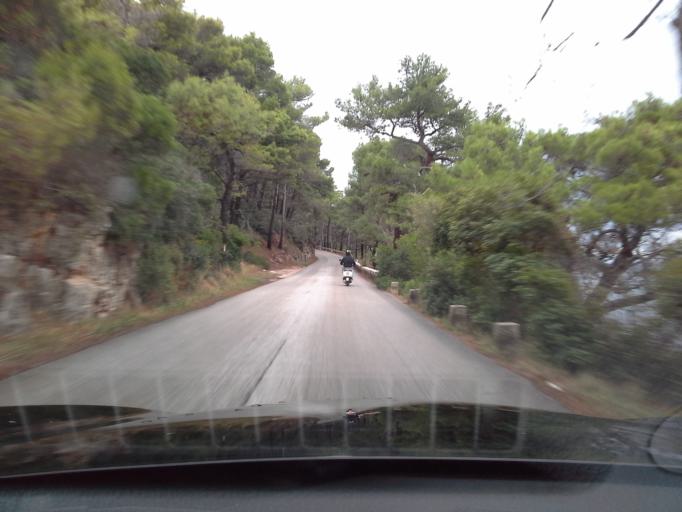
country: HR
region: Primorsko-Goranska
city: Mali Losinj
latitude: 44.5243
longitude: 14.4896
